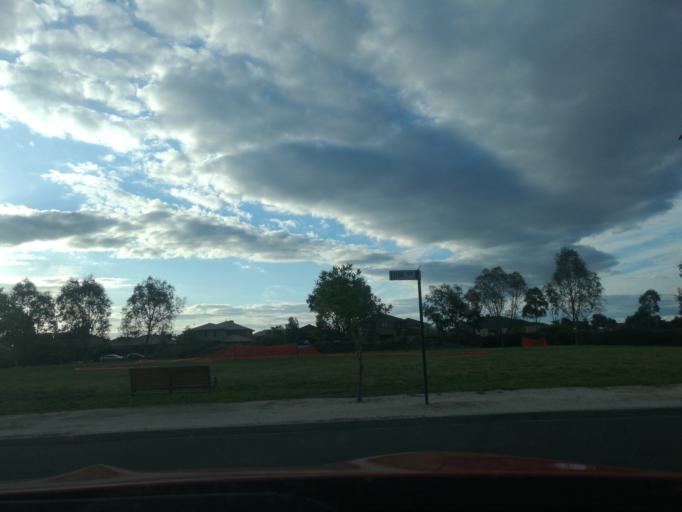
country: AU
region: Victoria
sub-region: Wyndham
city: Point Cook
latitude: -37.9141
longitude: 144.7784
